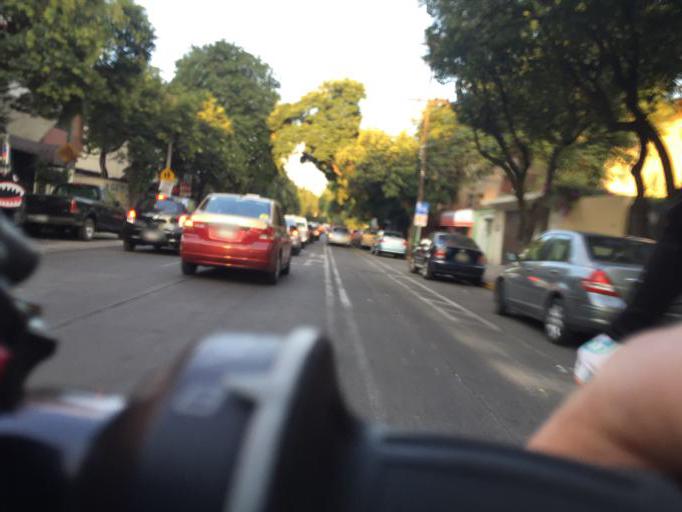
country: MX
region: Mexico City
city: Coyoacan
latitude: 19.3546
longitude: -99.1546
